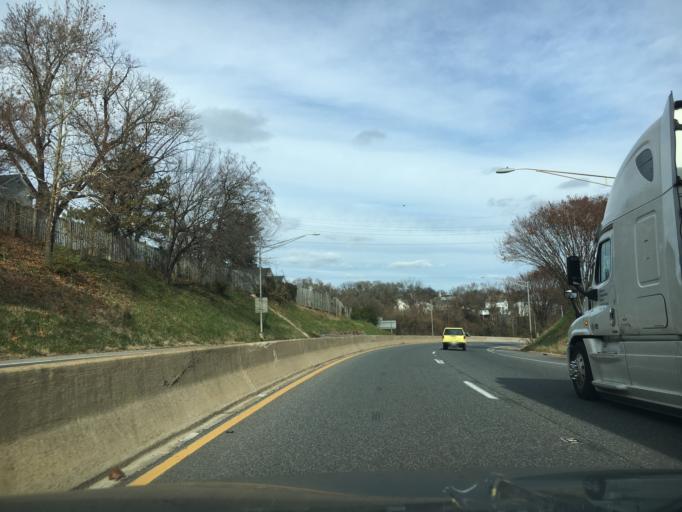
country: US
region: Virginia
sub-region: City of Lynchburg
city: Lynchburg
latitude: 37.3969
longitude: -79.1561
